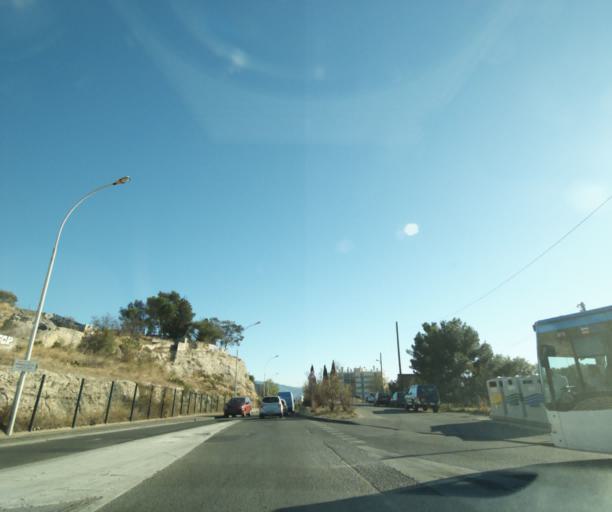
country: FR
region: Provence-Alpes-Cote d'Azur
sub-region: Departement des Bouches-du-Rhone
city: Marseille 14
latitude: 43.3561
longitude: 5.3697
